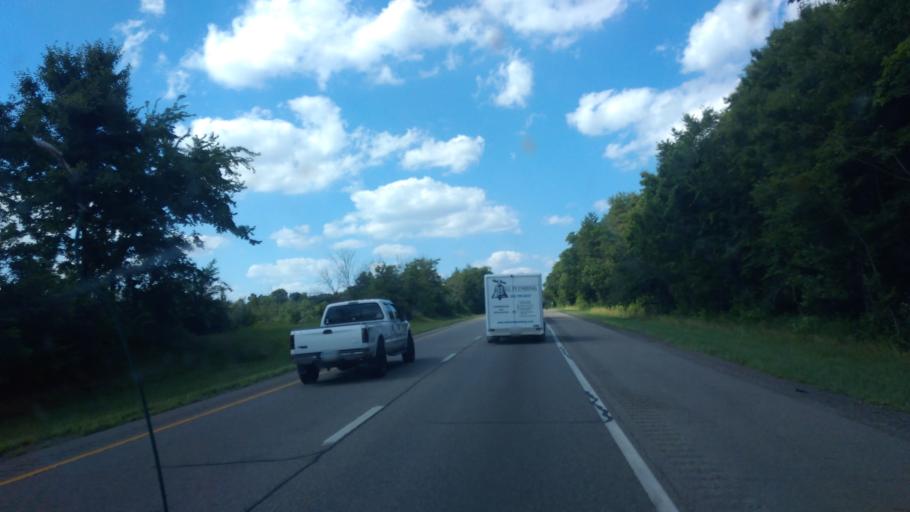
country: US
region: Ohio
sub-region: Stark County
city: Richville
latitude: 40.6910
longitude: -81.4321
